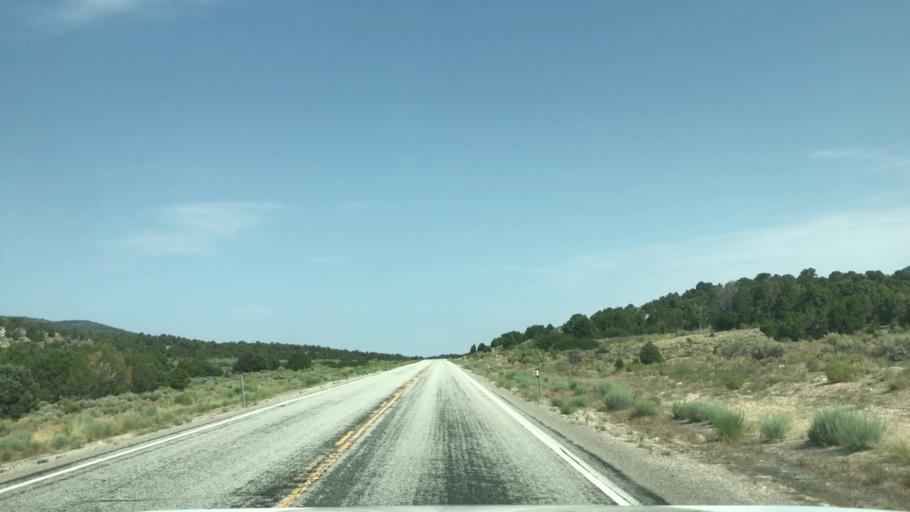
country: US
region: Nevada
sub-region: White Pine County
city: McGill
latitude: 39.1276
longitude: -114.3174
